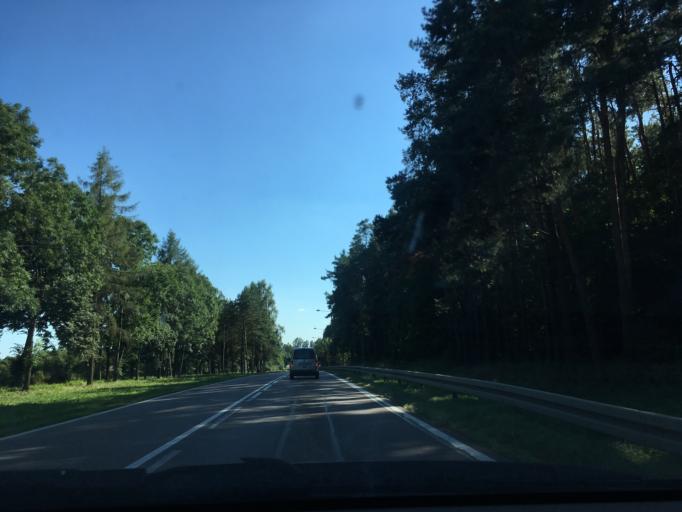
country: PL
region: Podlasie
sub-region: Powiat sokolski
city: Suchowola
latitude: 53.5551
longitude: 23.1002
